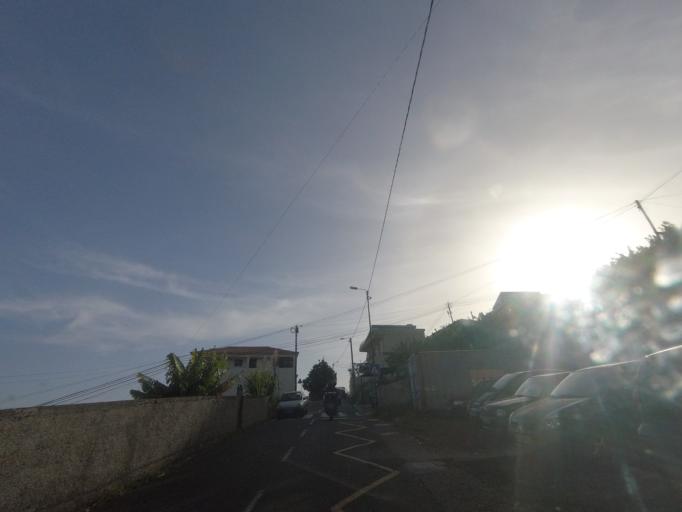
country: PT
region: Madeira
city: Camara de Lobos
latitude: 32.6541
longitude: -16.9898
